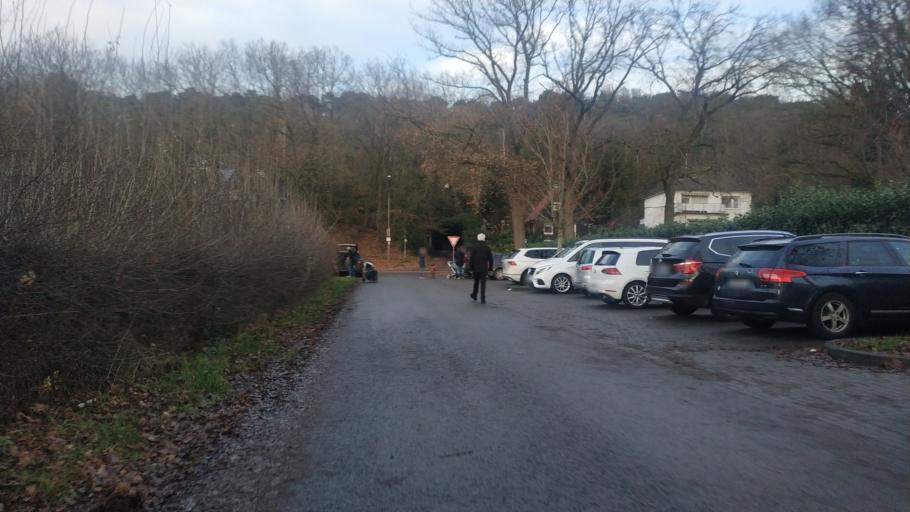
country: DE
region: North Rhine-Westphalia
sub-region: Regierungsbezirk Munster
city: Horstel
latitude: 52.2782
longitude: 7.6004
